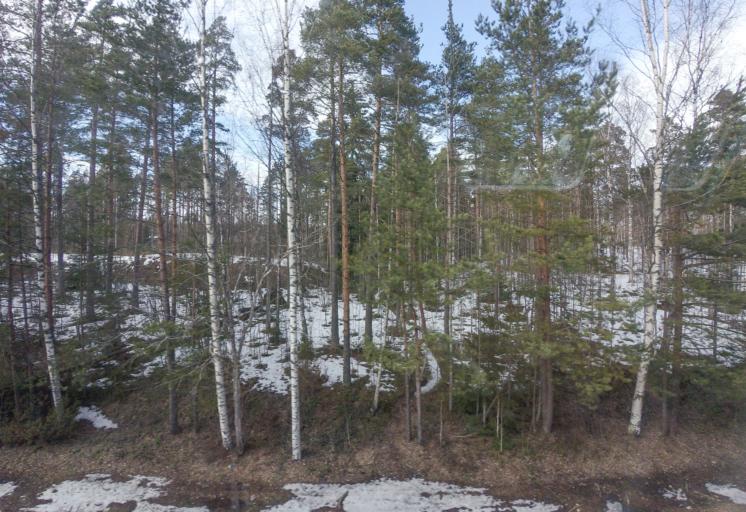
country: FI
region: South Karelia
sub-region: Lappeenranta
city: Joutseno
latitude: 61.1150
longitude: 28.4691
